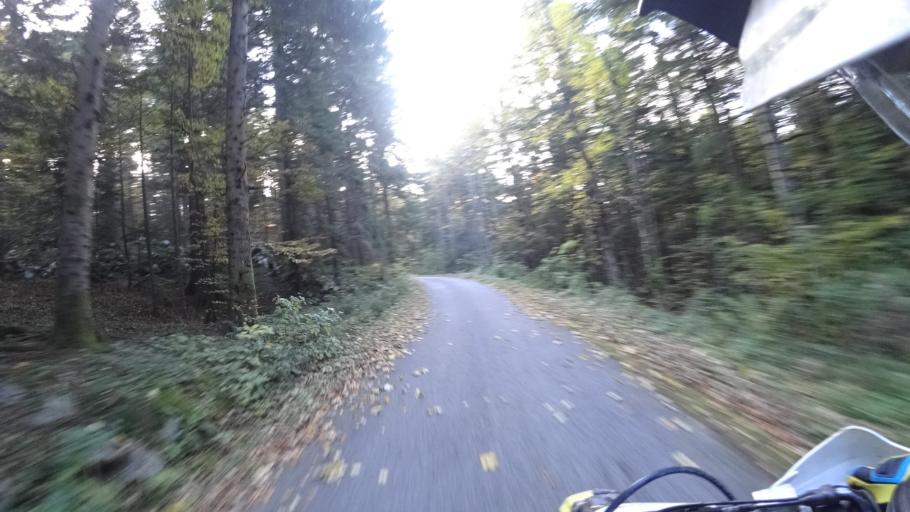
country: HR
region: Karlovacka
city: Plaski
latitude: 44.9802
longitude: 15.4150
